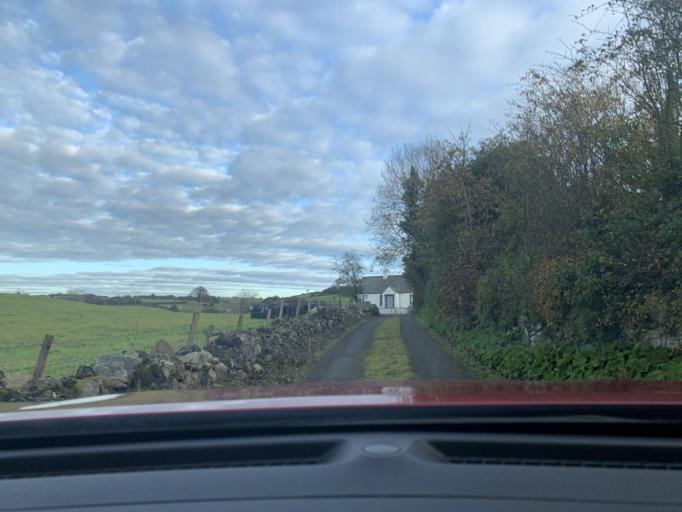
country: IE
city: Ballisodare
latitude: 54.2331
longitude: -8.5034
